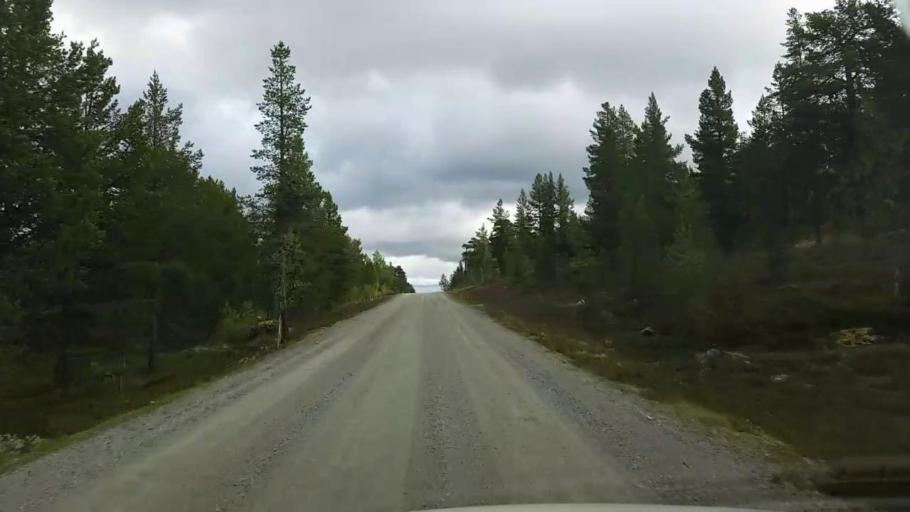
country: NO
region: Hedmark
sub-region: Engerdal
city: Engerdal
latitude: 62.3354
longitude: 12.6296
